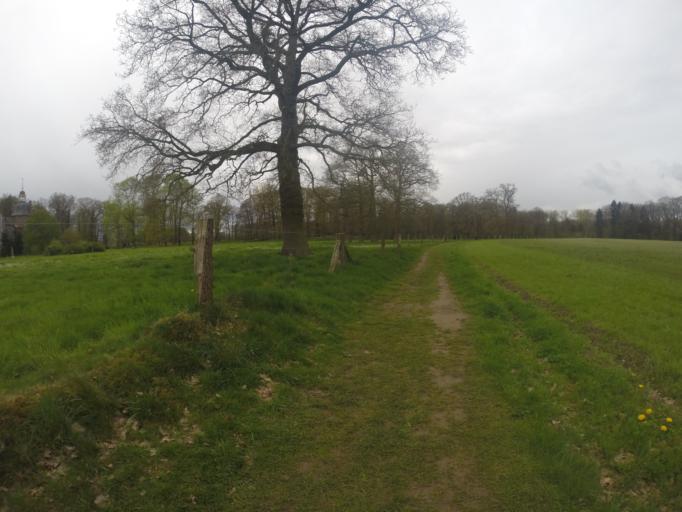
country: NL
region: Gelderland
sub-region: Gemeente Zutphen
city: Leesten
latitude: 52.1013
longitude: 6.2767
